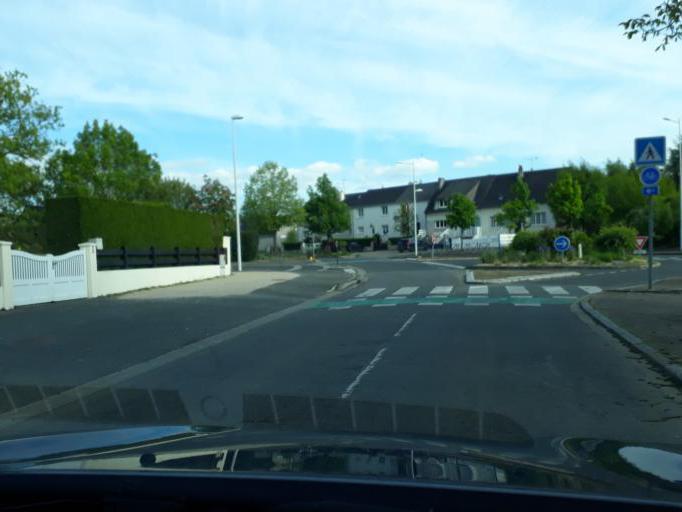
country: FR
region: Centre
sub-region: Departement du Loiret
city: Ingre
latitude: 47.9170
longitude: 1.8344
